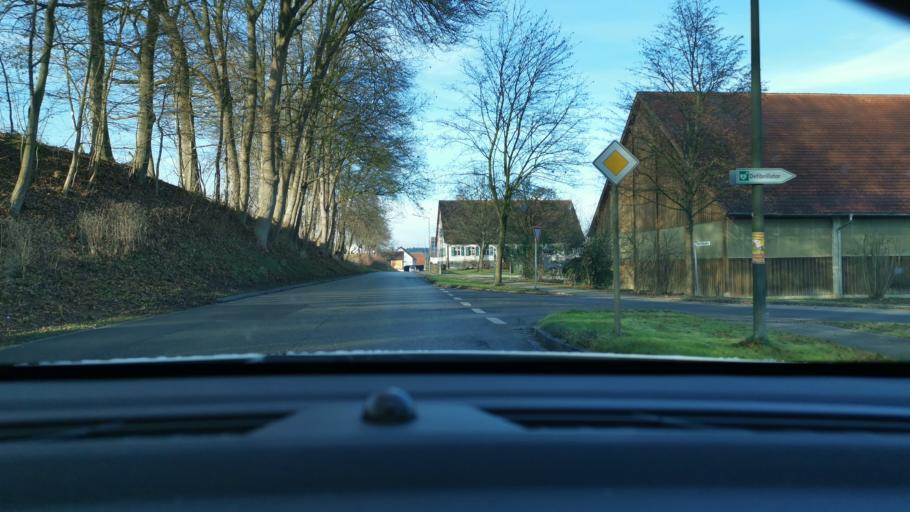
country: DE
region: Bavaria
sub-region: Swabia
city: Hollenbach
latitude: 48.5028
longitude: 11.0629
